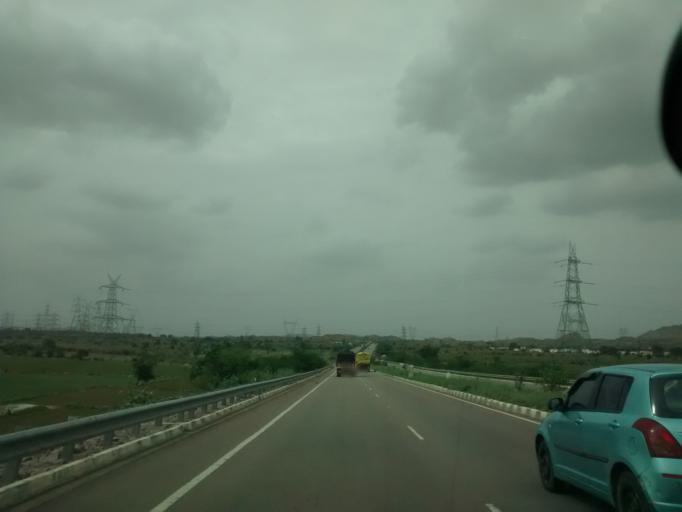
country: IN
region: Andhra Pradesh
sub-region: Kurnool
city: Ramapuram
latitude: 15.1370
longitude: 77.6624
